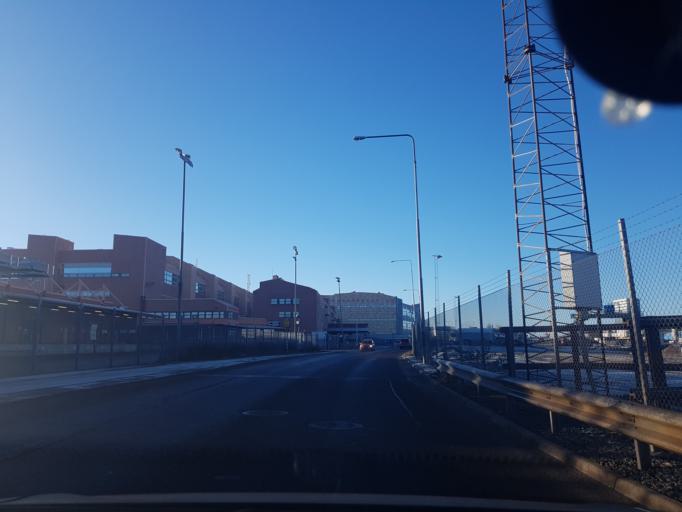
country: SE
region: Vaestra Goetaland
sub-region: Goteborg
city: Goeteborg
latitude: 57.7133
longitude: 11.9858
